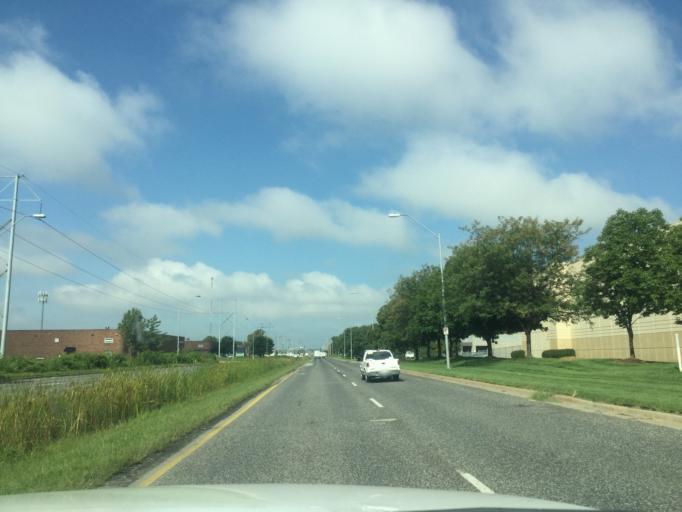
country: US
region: Missouri
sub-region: Clay County
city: North Kansas City
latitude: 39.1304
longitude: -94.5089
